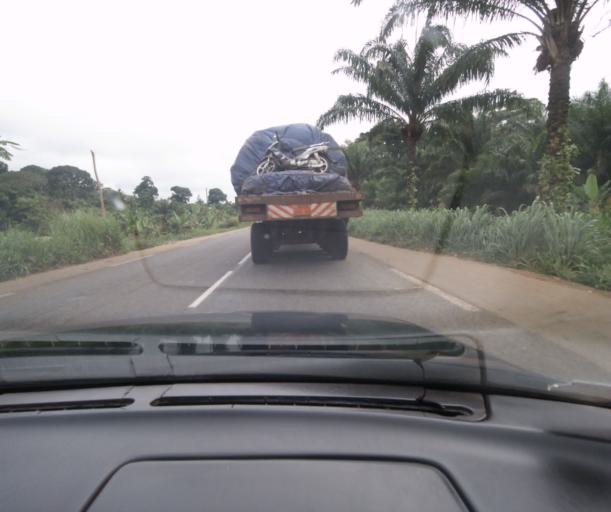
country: CM
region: Centre
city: Ombesa
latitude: 4.5881
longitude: 11.2641
